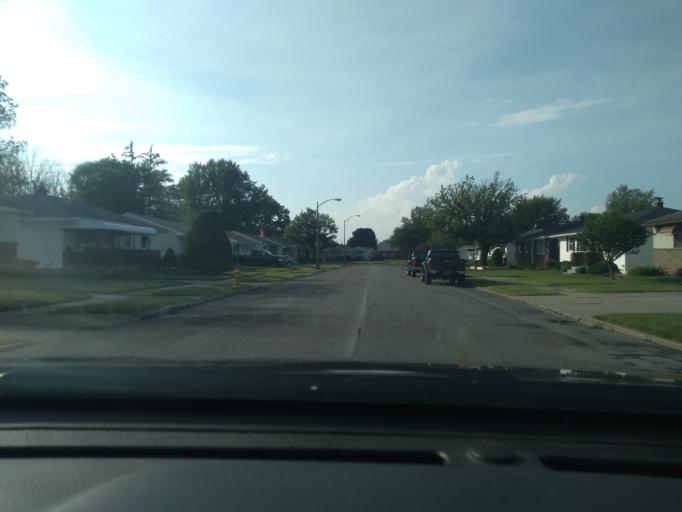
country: US
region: New York
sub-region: Erie County
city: Lackawanna
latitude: 42.8214
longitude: -78.8121
